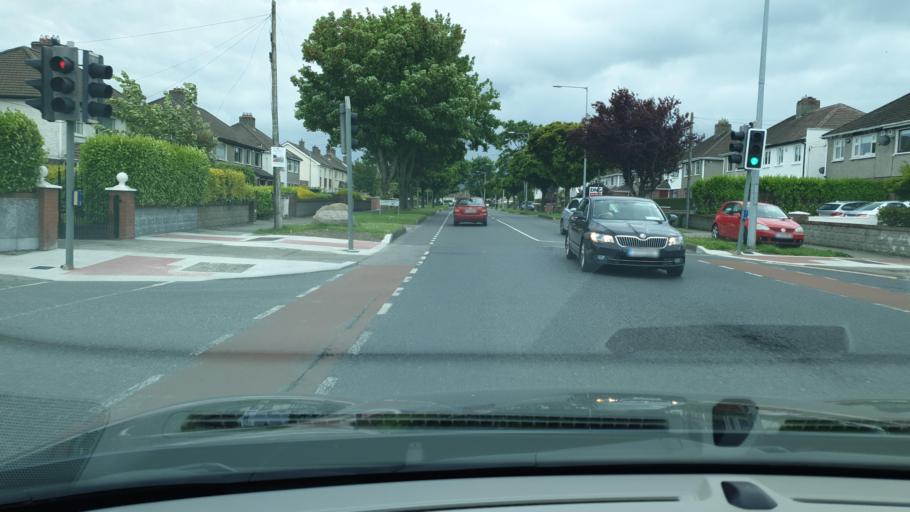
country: IE
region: Leinster
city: Crumlin
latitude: 53.3102
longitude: -6.3257
